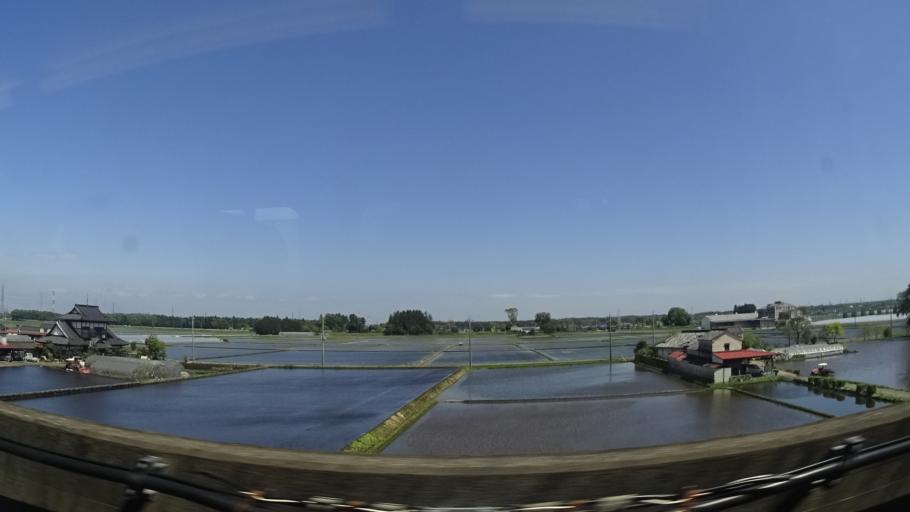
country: JP
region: Tochigi
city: Ujiie
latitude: 36.6480
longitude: 139.9120
